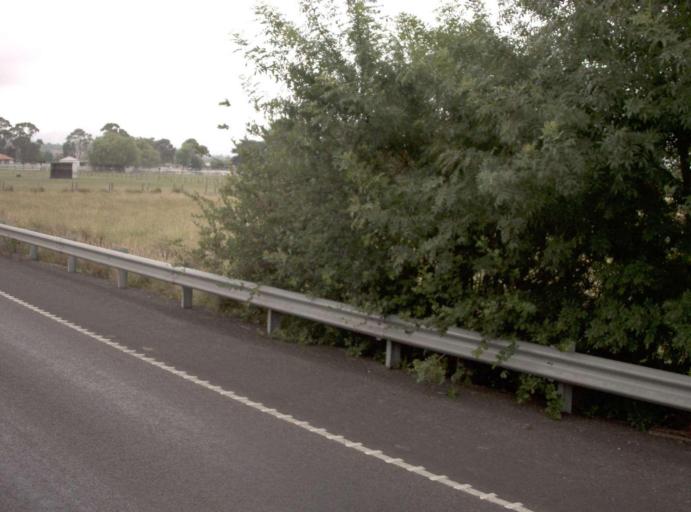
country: AU
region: Victoria
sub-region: Latrobe
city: Morwell
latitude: -38.2941
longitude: 146.4162
